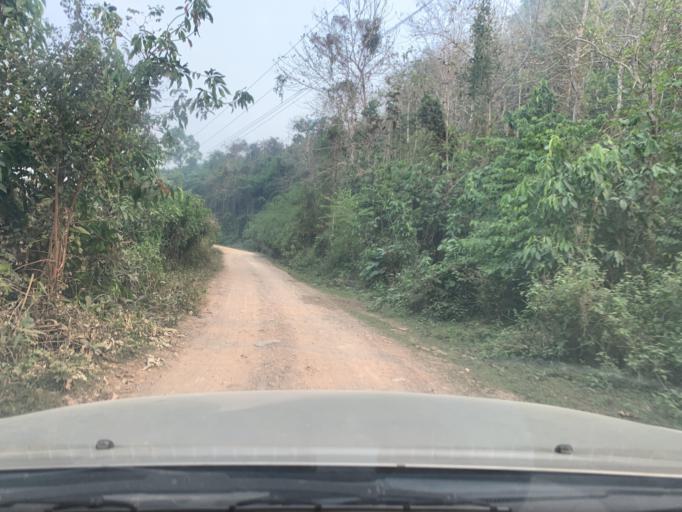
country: LA
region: Louangphabang
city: Louangphabang
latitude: 19.9231
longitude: 102.0742
